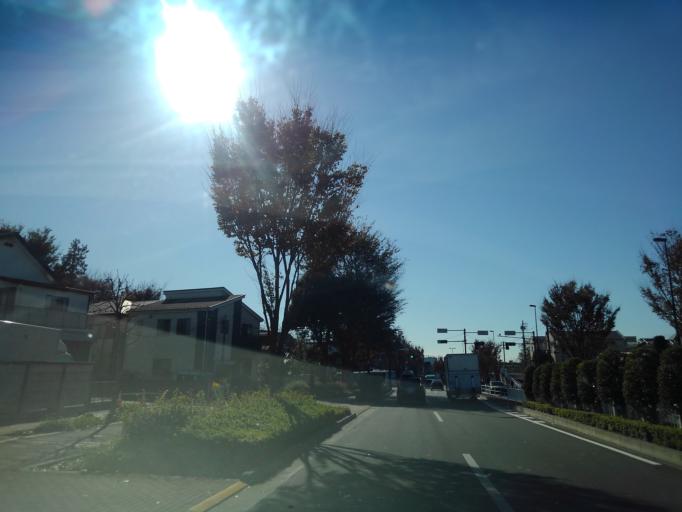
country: JP
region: Tokyo
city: Chofugaoka
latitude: 35.6688
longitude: 139.5446
